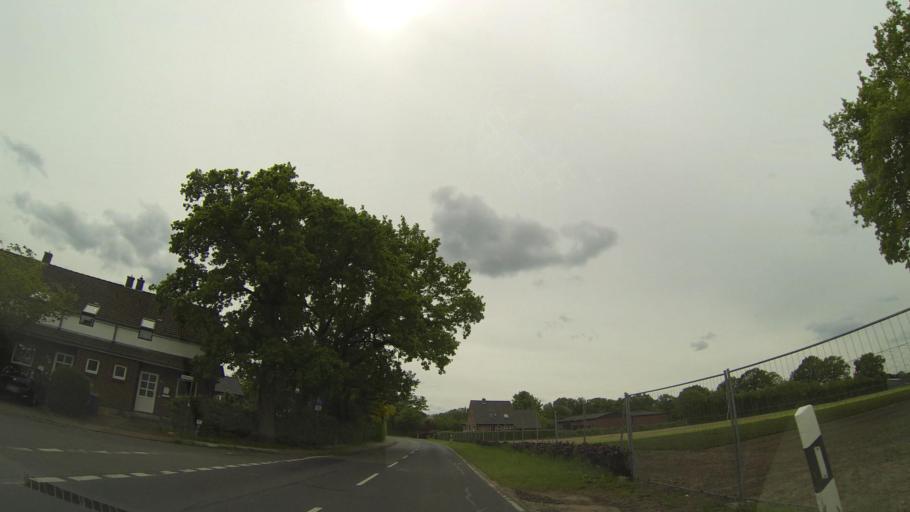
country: DE
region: Schleswig-Holstein
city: Ellerbek
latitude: 53.6435
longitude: 9.8705
